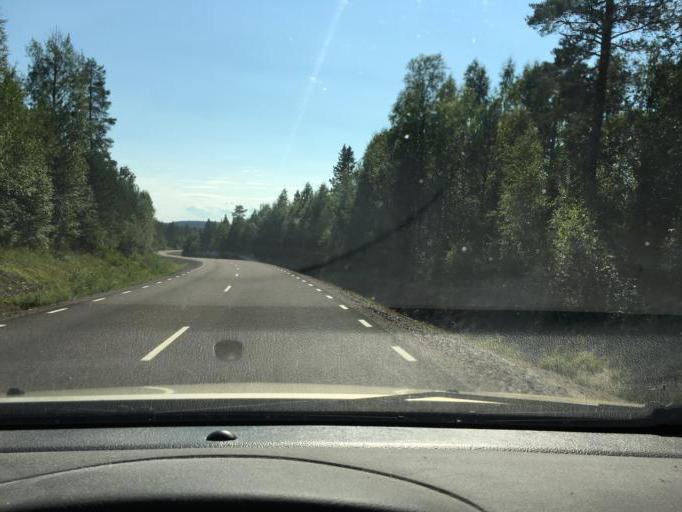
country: SE
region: Norrbotten
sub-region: Lulea Kommun
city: Ranea
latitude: 66.0411
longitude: 22.1838
